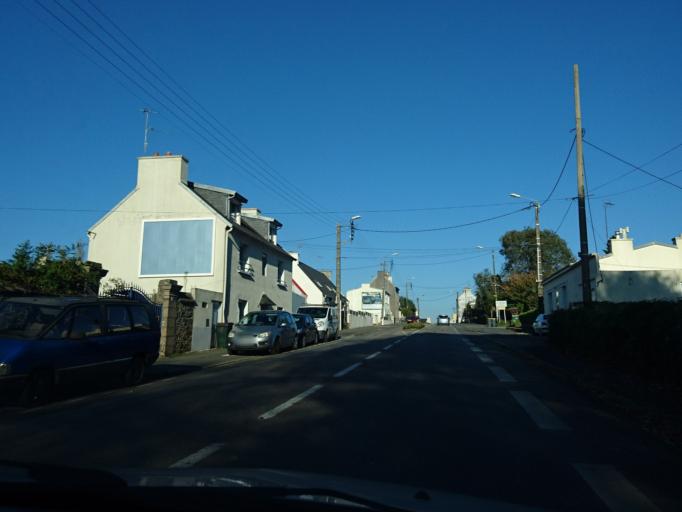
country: FR
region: Brittany
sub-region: Departement du Finistere
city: Brest
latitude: 48.4112
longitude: -4.4539
